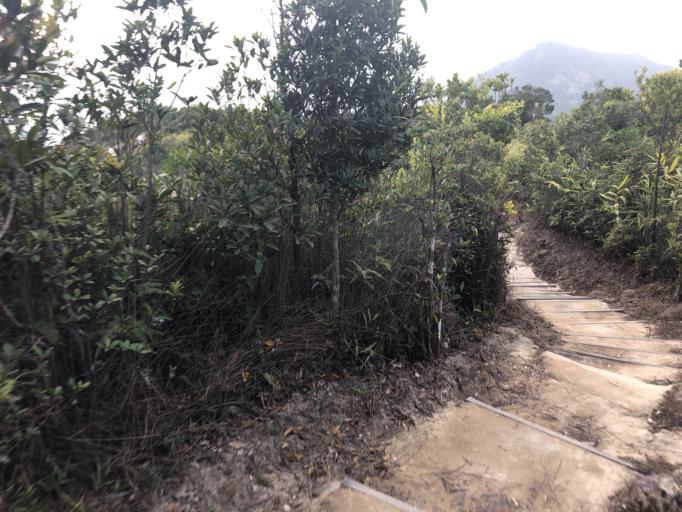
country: HK
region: Wanchai
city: Wan Chai
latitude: 22.2658
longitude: 114.1981
